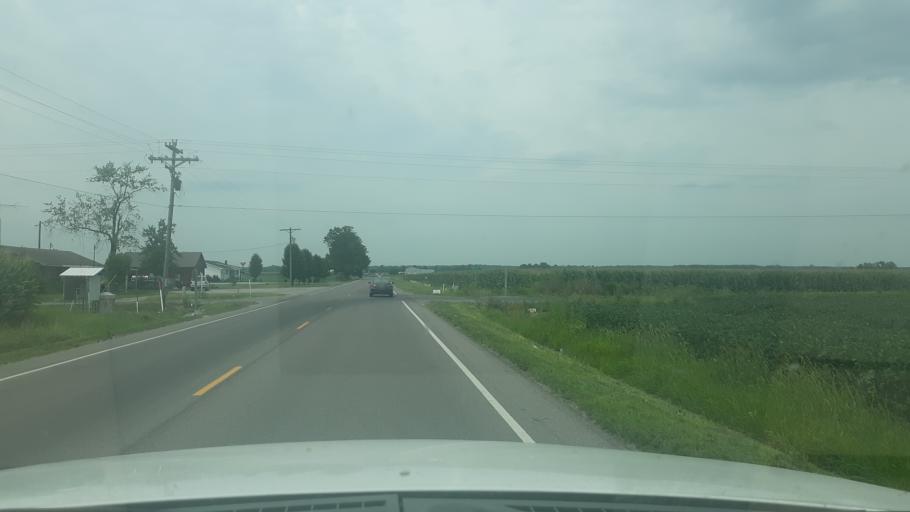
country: US
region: Illinois
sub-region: Saline County
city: Harrisburg
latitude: 37.8042
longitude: -88.5398
